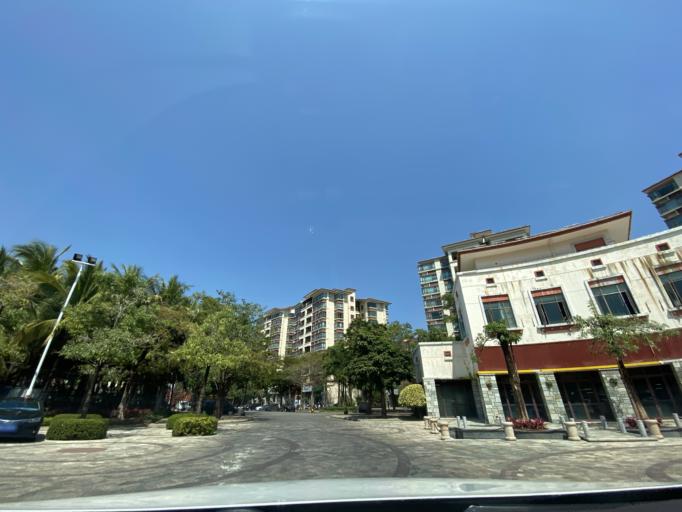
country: CN
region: Hainan
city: Yingzhou
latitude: 18.4061
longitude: 109.8507
